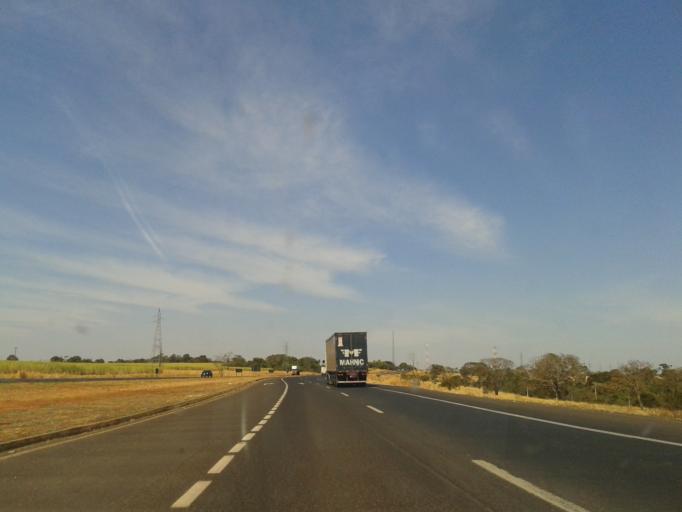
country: BR
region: Minas Gerais
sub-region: Centralina
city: Centralina
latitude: -18.7611
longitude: -49.0759
